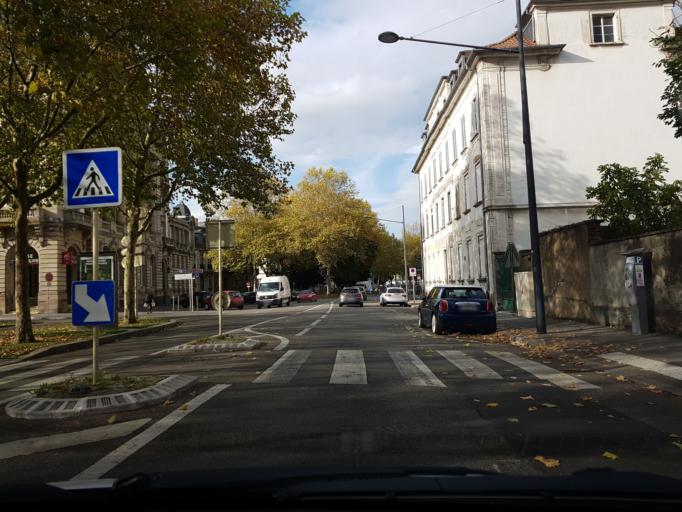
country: FR
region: Alsace
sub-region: Departement du Haut-Rhin
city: Mulhouse
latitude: 47.7479
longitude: 7.3318
